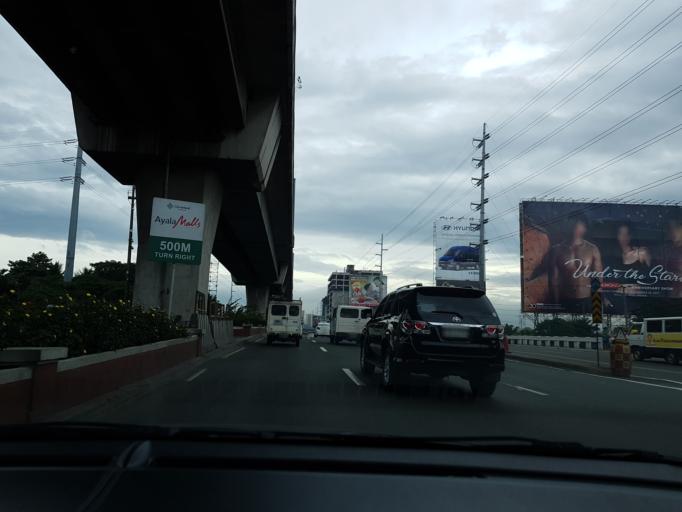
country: PH
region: Calabarzon
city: Del Monte
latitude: 14.6573
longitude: 120.9997
